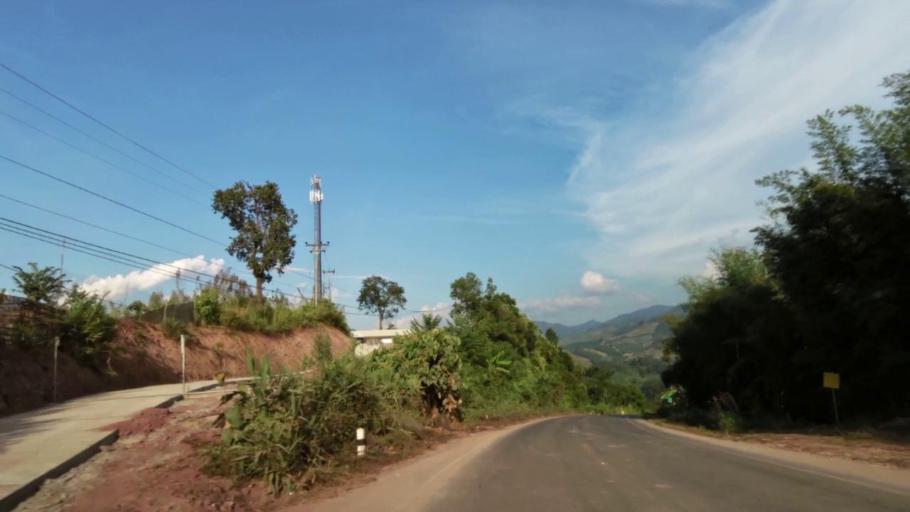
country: TH
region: Chiang Rai
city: Khun Tan
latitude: 19.8585
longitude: 100.3900
